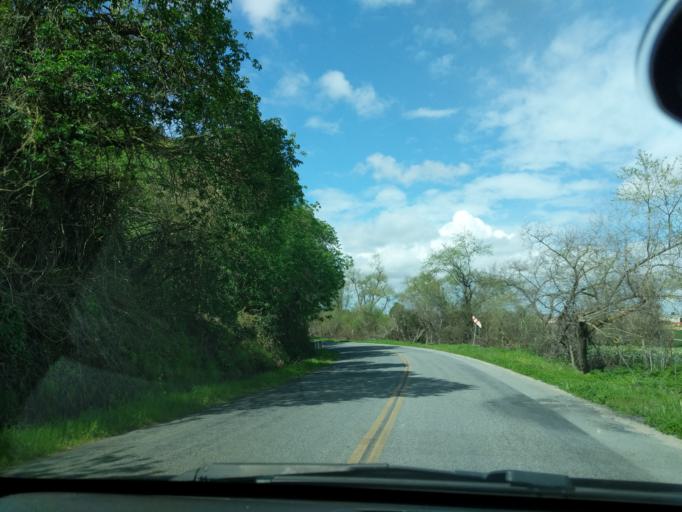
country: US
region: California
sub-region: Monterey County
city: Prunedale
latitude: 36.7578
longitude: -121.6042
